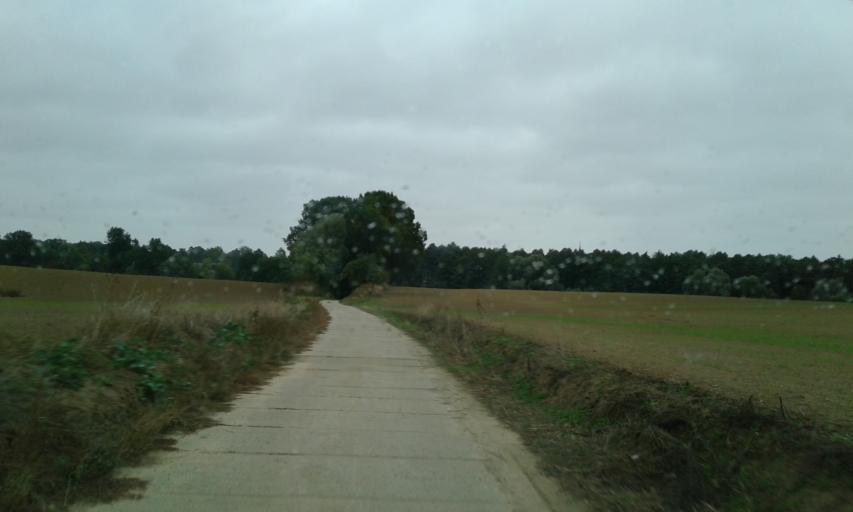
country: PL
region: West Pomeranian Voivodeship
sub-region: Powiat stargardzki
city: Dolice
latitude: 53.1065
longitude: 15.2245
